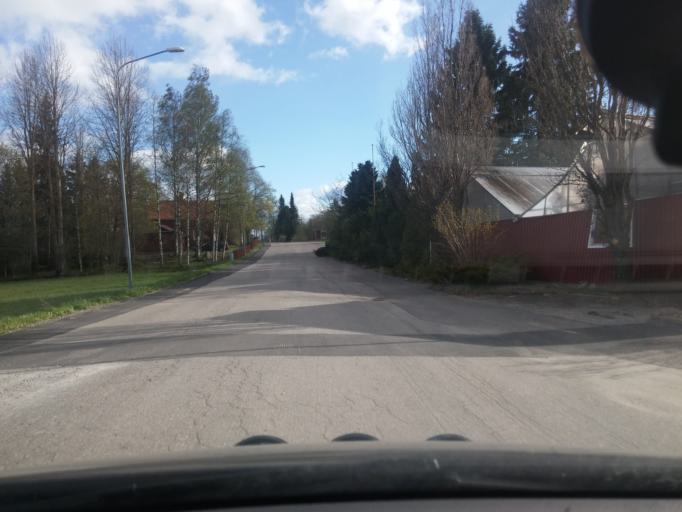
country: SE
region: Gaevleborg
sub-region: Bollnas Kommun
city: Arbra
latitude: 61.4859
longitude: 16.3714
